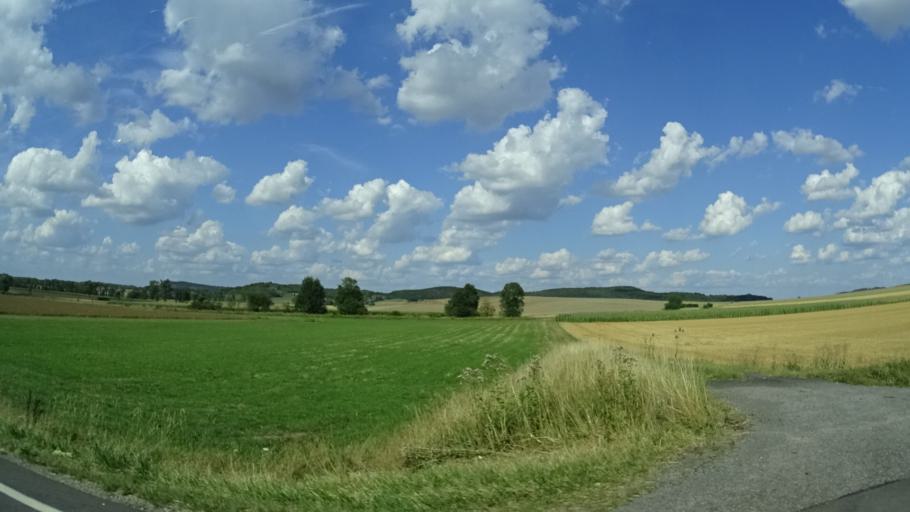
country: DE
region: Bavaria
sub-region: Regierungsbezirk Unterfranken
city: Bad Konigshofen im Grabfeld
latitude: 50.2819
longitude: 10.4915
